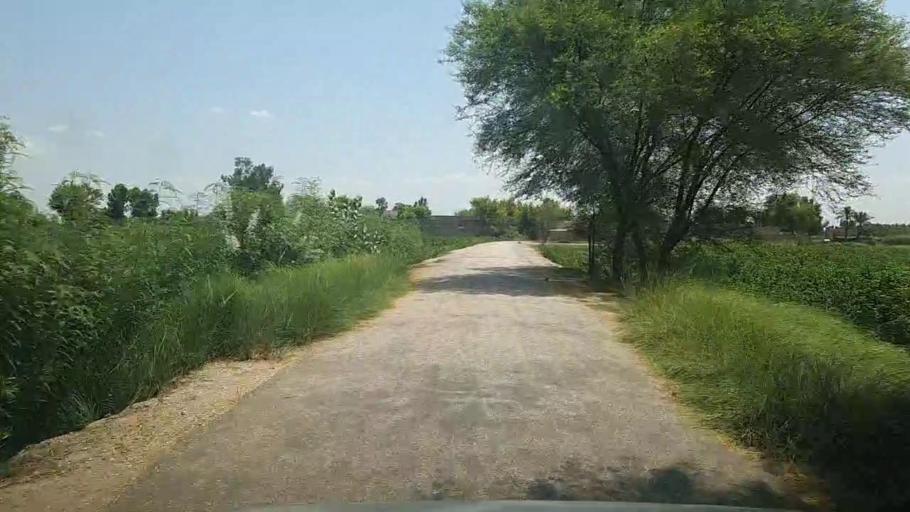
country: PK
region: Sindh
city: Ubauro
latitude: 28.1567
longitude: 69.7490
